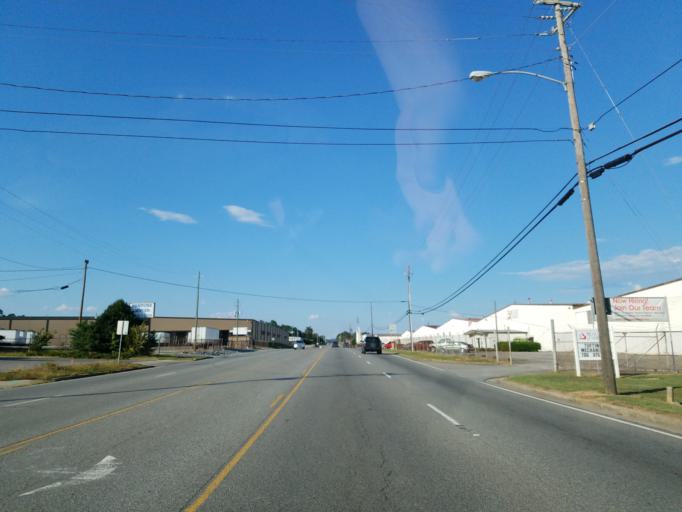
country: US
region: Georgia
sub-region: Murray County
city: Chatsworth
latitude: 34.8264
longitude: -84.7625
